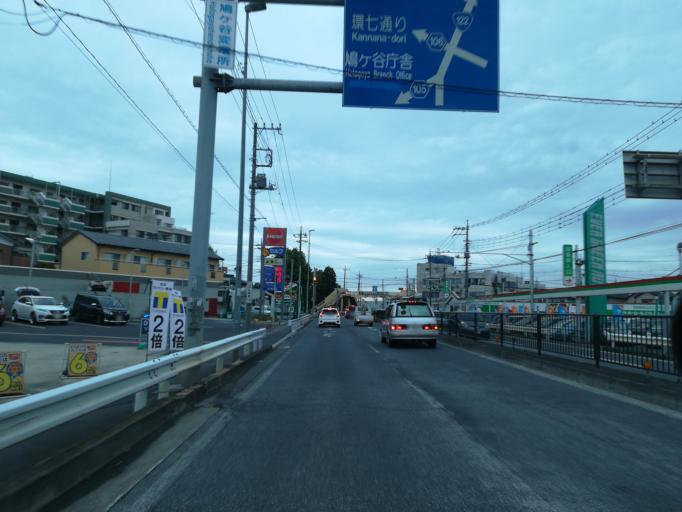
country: JP
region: Saitama
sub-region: Kawaguchi-shi
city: Hatogaya-honcho
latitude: 35.8244
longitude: 139.7380
